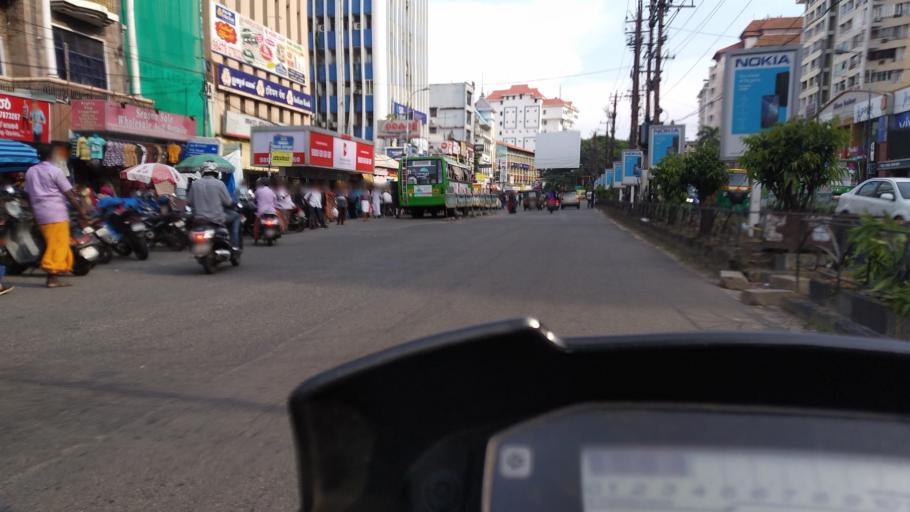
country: IN
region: Kerala
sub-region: Ernakulam
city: Cochin
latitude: 9.9781
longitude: 76.2768
